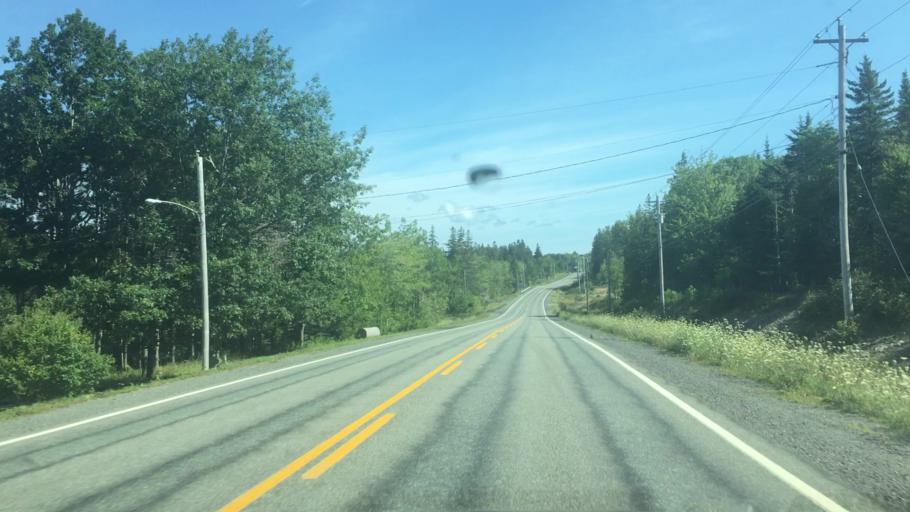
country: CA
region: Nova Scotia
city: Sydney
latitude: 45.9915
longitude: -60.4115
